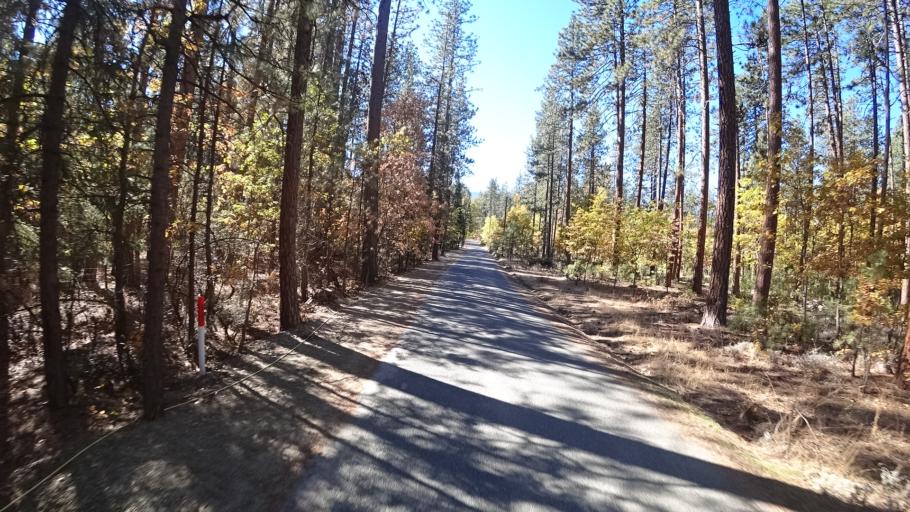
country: US
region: California
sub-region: Siskiyou County
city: Yreka
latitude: 41.5183
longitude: -122.9017
